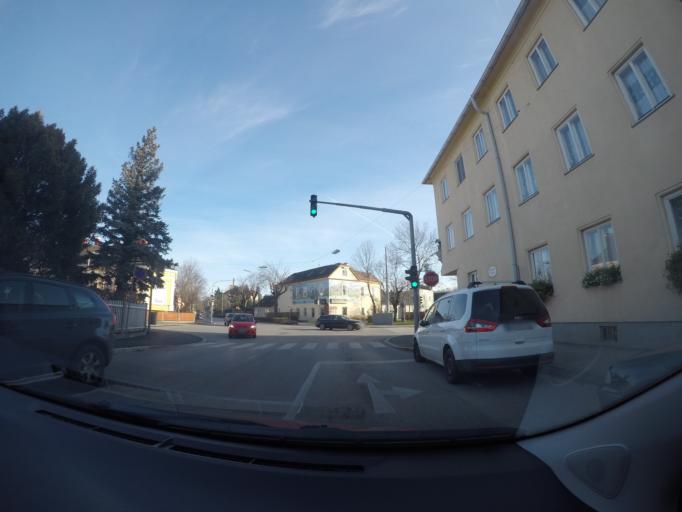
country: AT
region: Lower Austria
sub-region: Politischer Bezirk Baden
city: Baden
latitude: 48.0026
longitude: 16.2306
